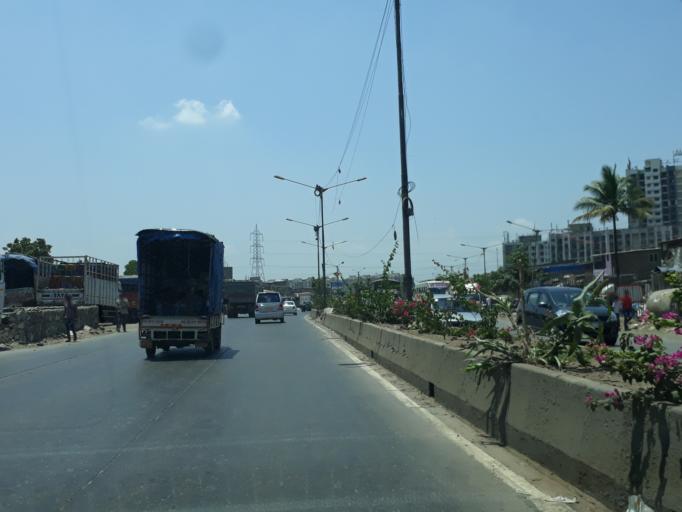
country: IN
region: Maharashtra
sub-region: Mumbai Suburban
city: Mumbai
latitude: 19.0552
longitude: 72.9336
